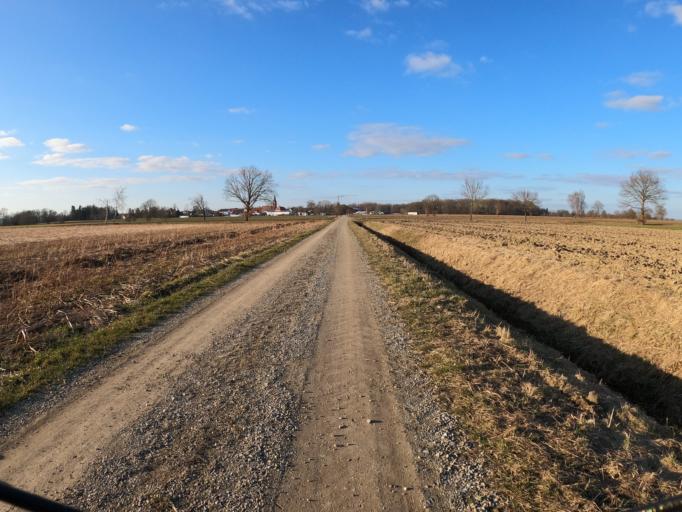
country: DE
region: Bavaria
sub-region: Swabia
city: Leipheim
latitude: 48.4212
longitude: 10.1996
